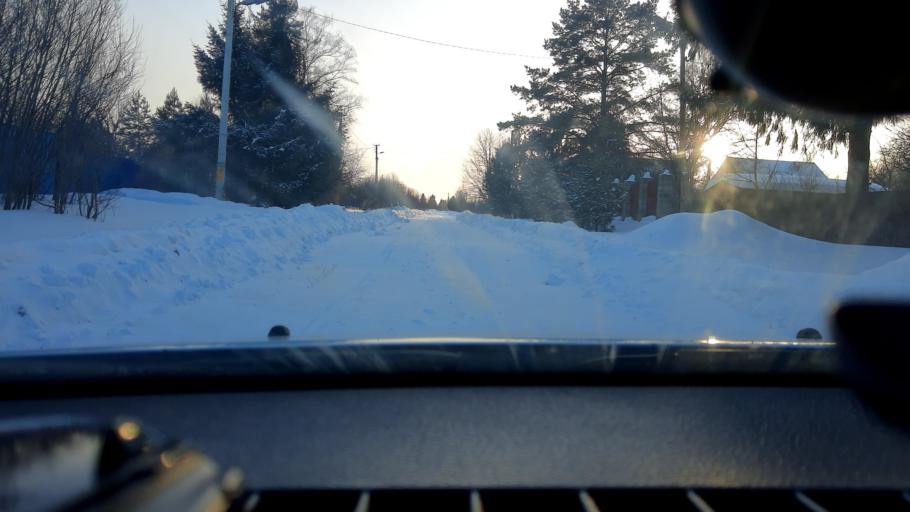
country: RU
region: Bashkortostan
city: Kudeyevskiy
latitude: 54.7951
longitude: 56.6734
